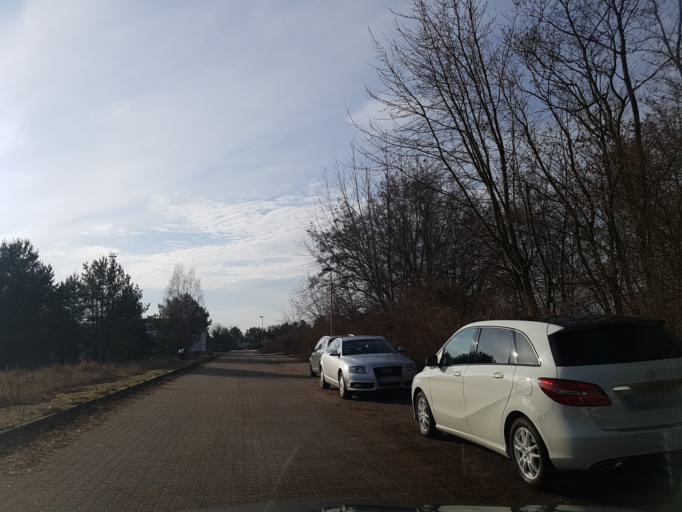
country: DE
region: Brandenburg
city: Bad Liebenwerda
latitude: 51.5303
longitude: 13.3915
